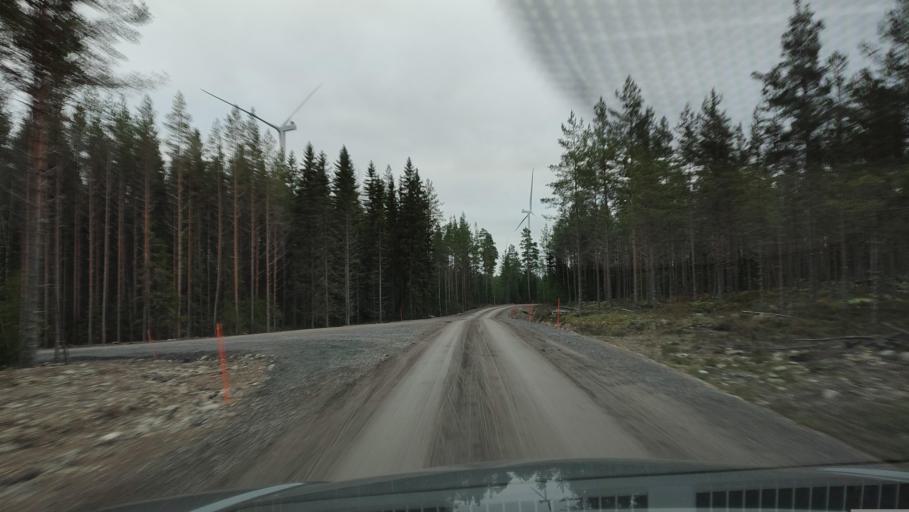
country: FI
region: Southern Ostrobothnia
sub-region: Suupohja
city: Karijoki
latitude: 62.1997
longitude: 21.5895
